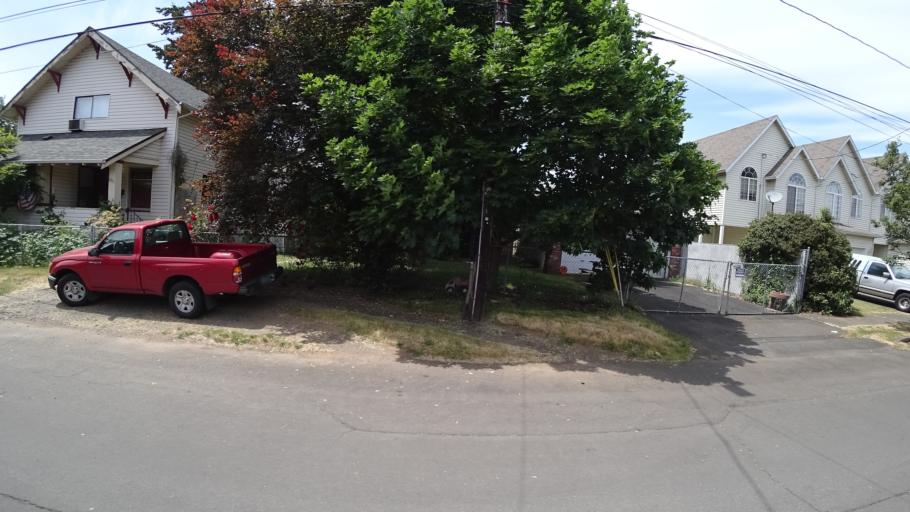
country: US
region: Oregon
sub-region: Multnomah County
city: Lents
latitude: 45.4753
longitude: -122.5943
